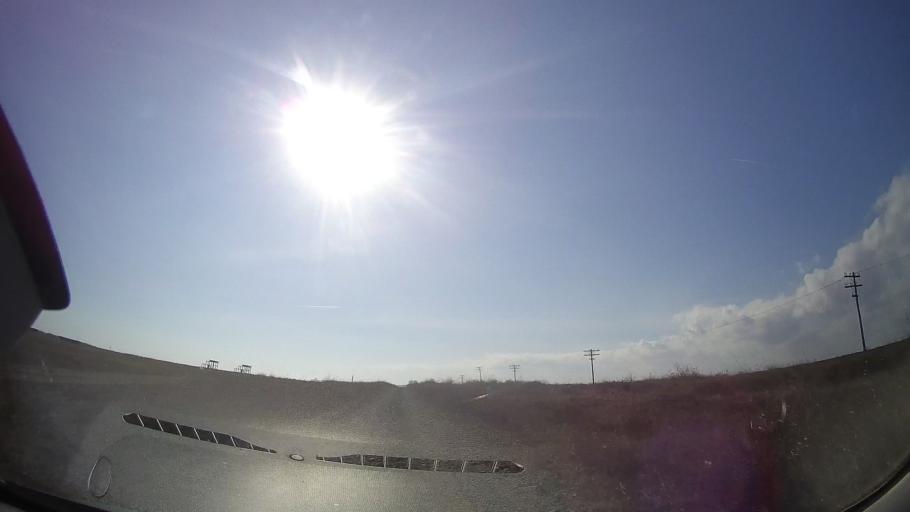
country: RO
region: Constanta
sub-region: Comuna Costinesti
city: Schitu
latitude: 43.9191
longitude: 28.6294
